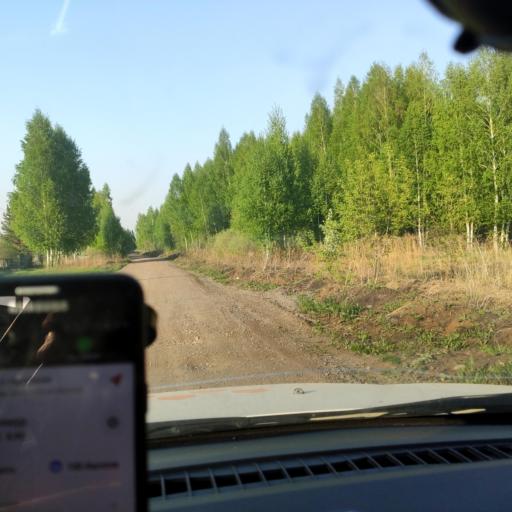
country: RU
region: Bashkortostan
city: Kabakovo
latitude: 54.7256
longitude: 56.2259
